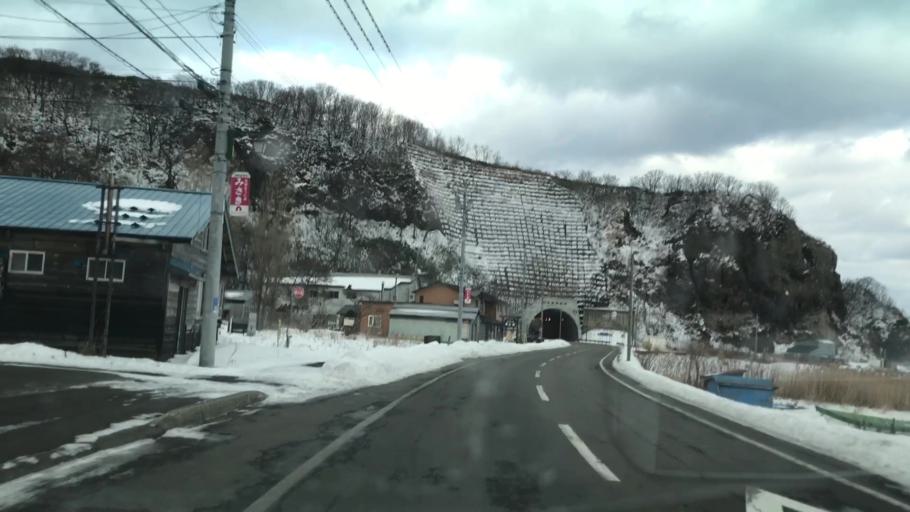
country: JP
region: Hokkaido
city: Iwanai
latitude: 43.3301
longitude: 140.3959
